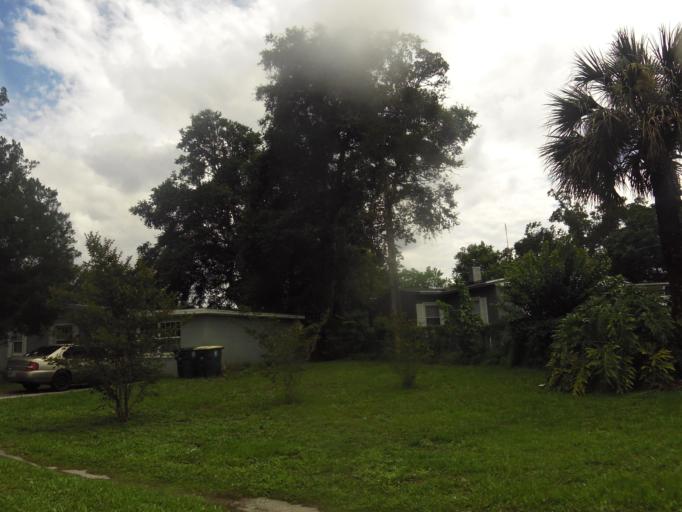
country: US
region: Florida
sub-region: Duval County
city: Jacksonville
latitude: 30.2854
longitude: -81.5547
